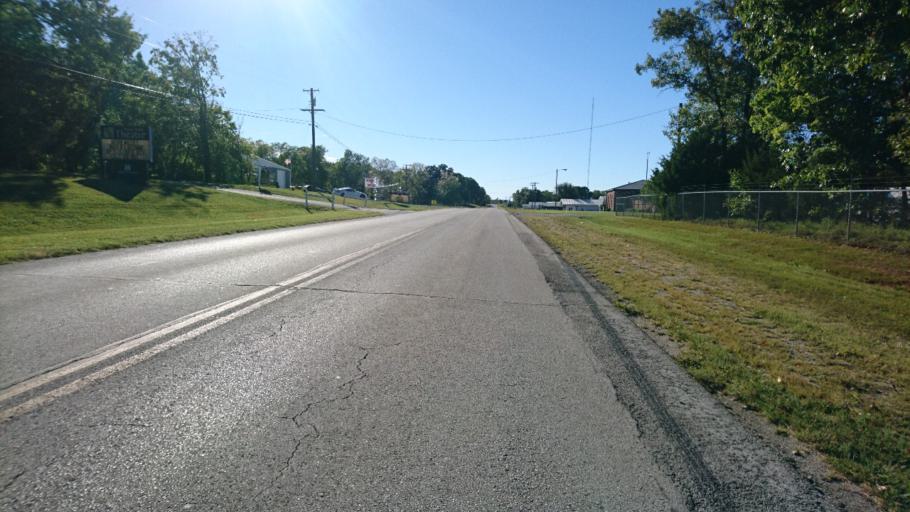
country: US
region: Missouri
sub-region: Jasper County
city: Carthage
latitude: 37.1732
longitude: -94.3525
